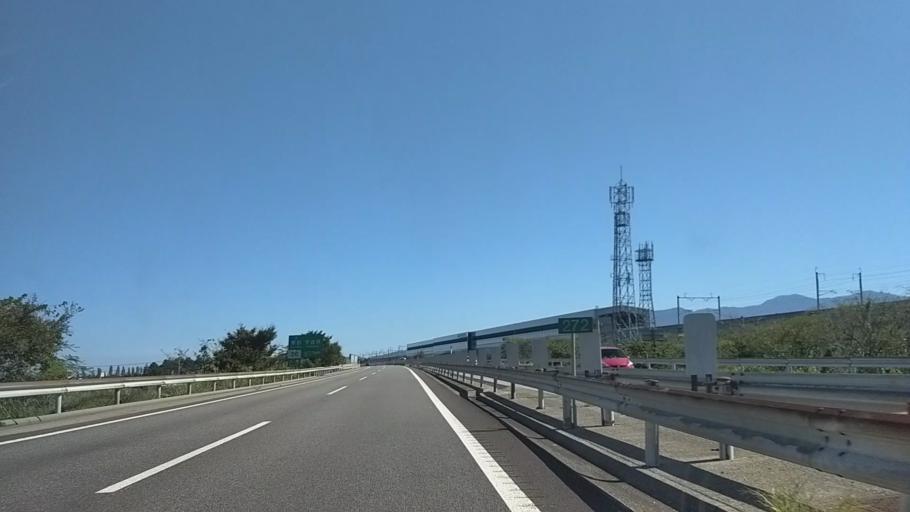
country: JP
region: Toyama
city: Nyuzen
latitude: 36.8721
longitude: 137.4773
